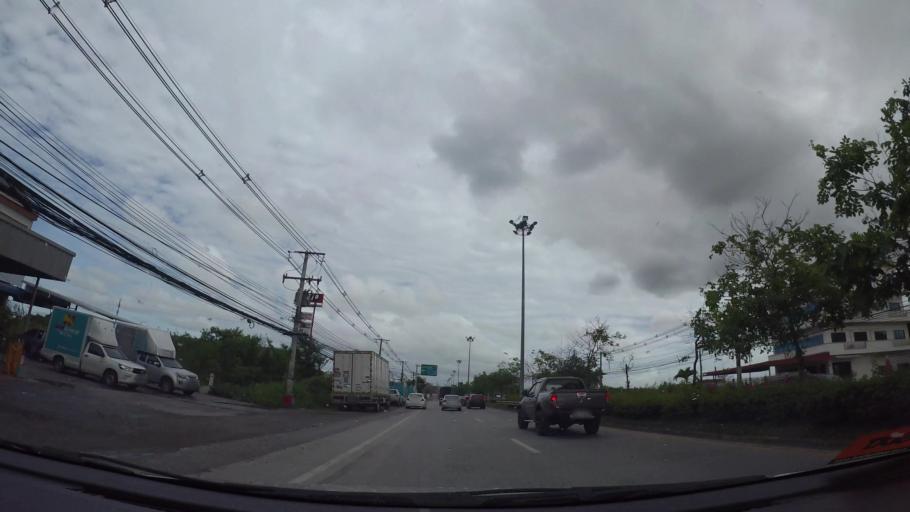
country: TH
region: Rayong
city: Rayong
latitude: 12.6992
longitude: 101.1920
